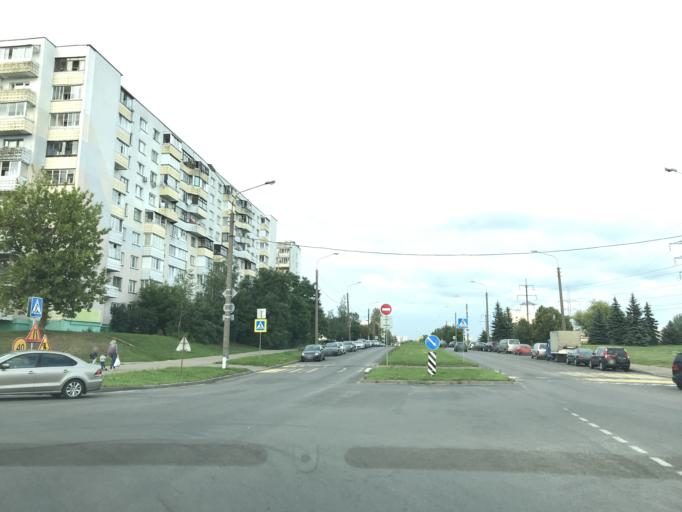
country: BY
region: Minsk
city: Minsk
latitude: 53.9493
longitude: 27.6015
